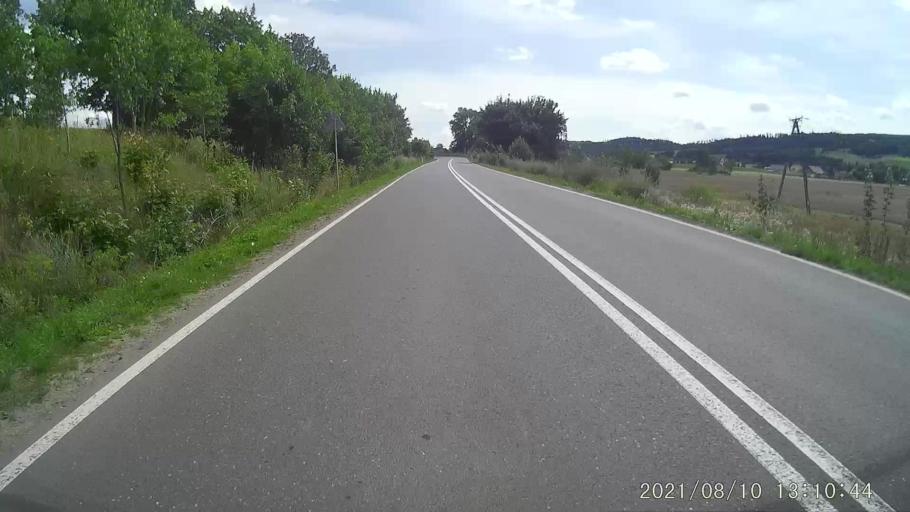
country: PL
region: Lower Silesian Voivodeship
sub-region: Powiat klodzki
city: Bozkow
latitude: 50.5042
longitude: 16.5252
